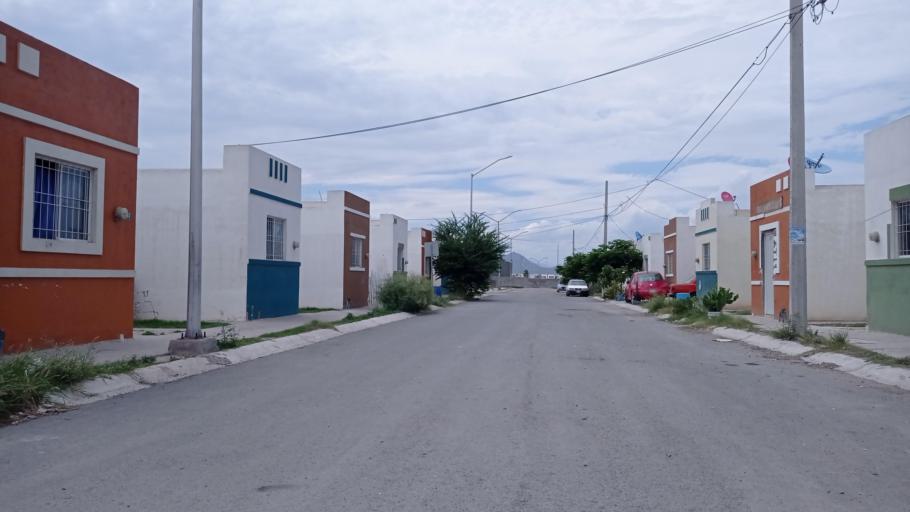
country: MX
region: Nuevo Leon
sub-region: Salinas Victoria
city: Simeprodeso (Colectivo Nuevo)
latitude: 25.8758
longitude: -100.3161
